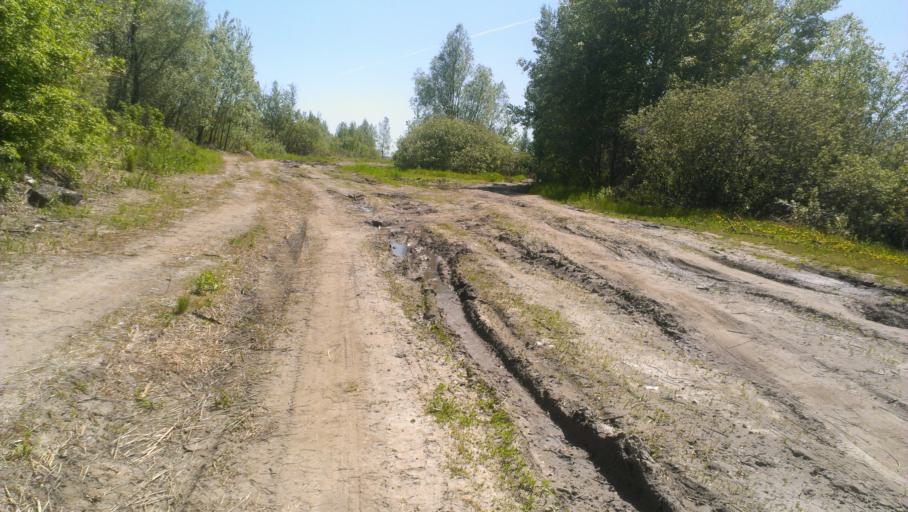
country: RU
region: Altai Krai
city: Zaton
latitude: 53.3141
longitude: 83.8513
